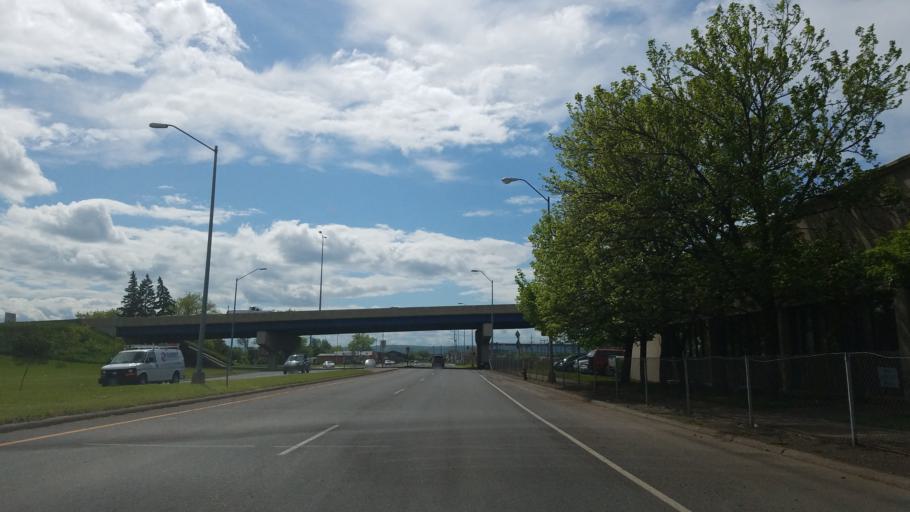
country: US
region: Wisconsin
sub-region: Douglas County
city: Superior
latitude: 46.7351
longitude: -92.0957
